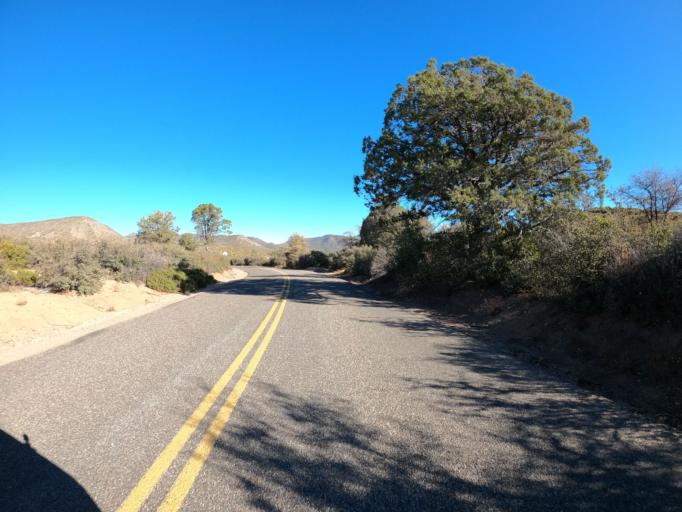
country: US
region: Arizona
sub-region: Yavapai County
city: Verde Village
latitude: 34.5705
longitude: -112.0736
